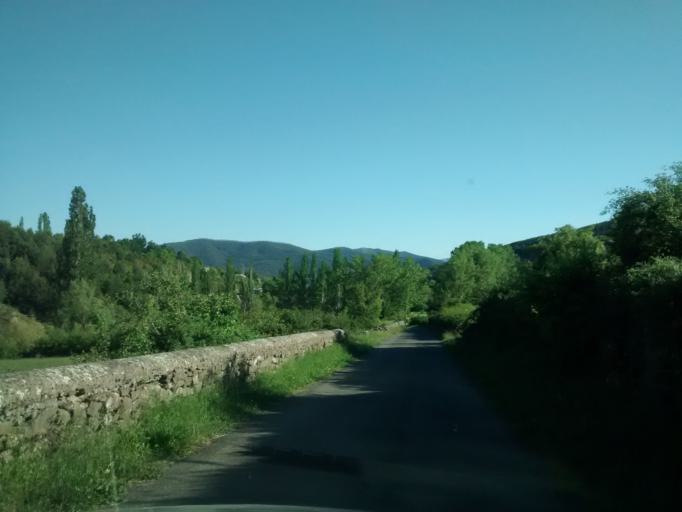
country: ES
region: Aragon
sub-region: Provincia de Huesca
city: Jasa
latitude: 42.6898
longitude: -0.6214
